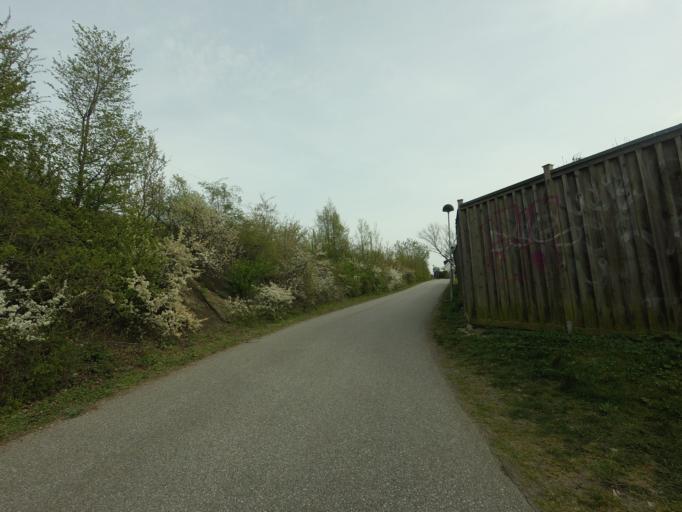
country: SE
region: Skane
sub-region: Lunds Kommun
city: Lund
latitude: 55.7189
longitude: 13.1768
